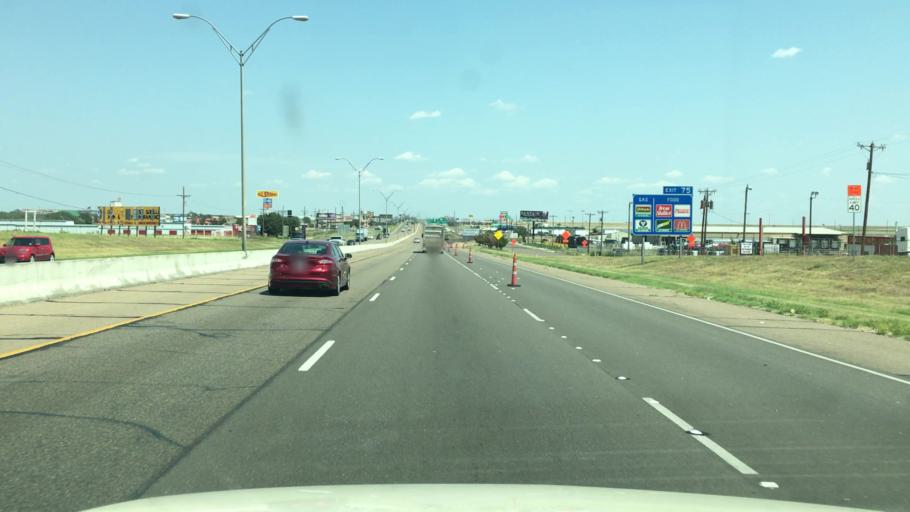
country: US
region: Texas
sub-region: Potter County
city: Amarillo
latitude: 35.1927
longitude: -101.7521
